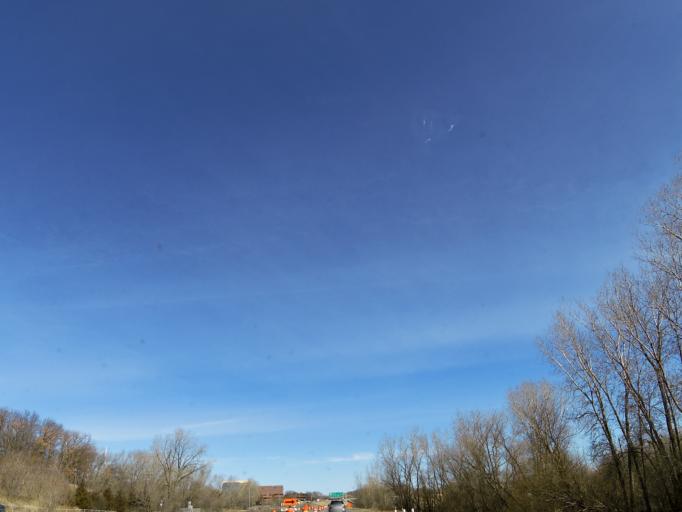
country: US
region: Minnesota
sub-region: Hennepin County
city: Eden Prairie
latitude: 44.8757
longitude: -93.4149
